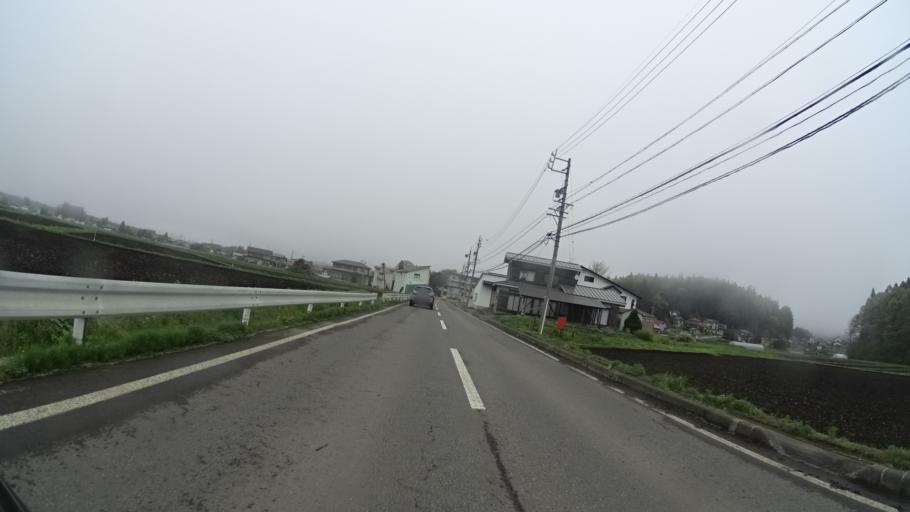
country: JP
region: Nagano
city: Nagano-shi
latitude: 36.7726
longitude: 138.2016
